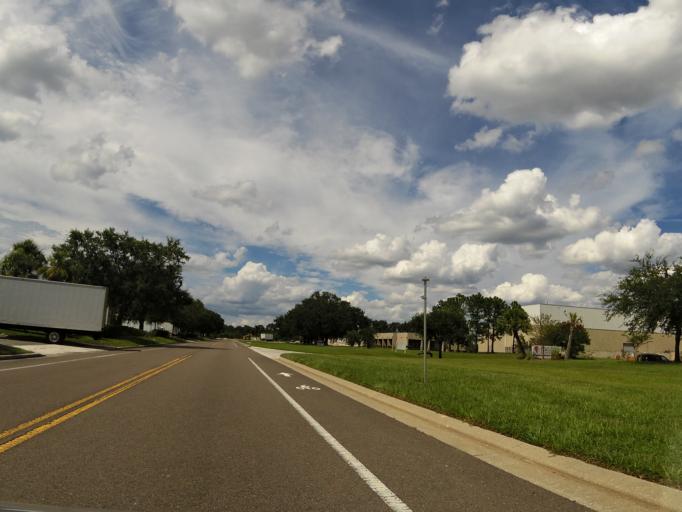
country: US
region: Florida
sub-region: Duval County
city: Jacksonville
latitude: 30.4234
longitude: -81.6359
